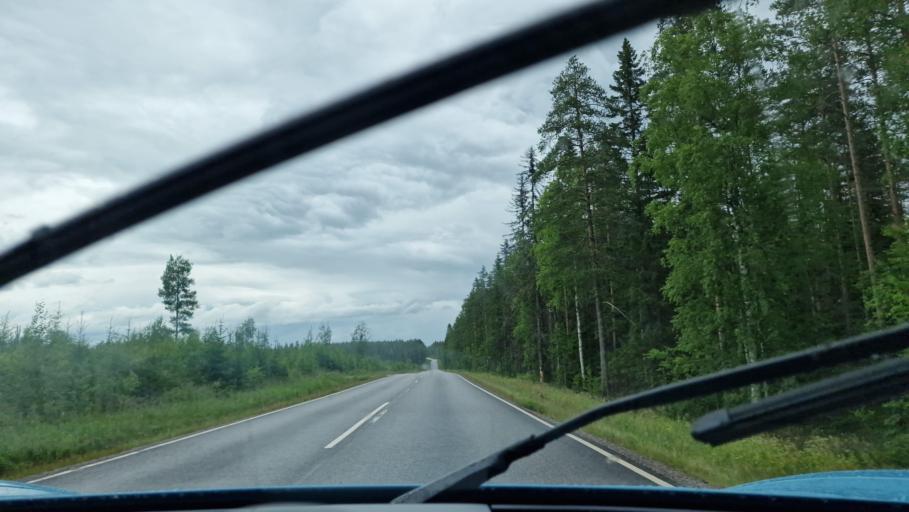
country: FI
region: Central Finland
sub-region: Saarijaervi-Viitasaari
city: Pylkoenmaeki
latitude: 62.6049
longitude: 24.5853
